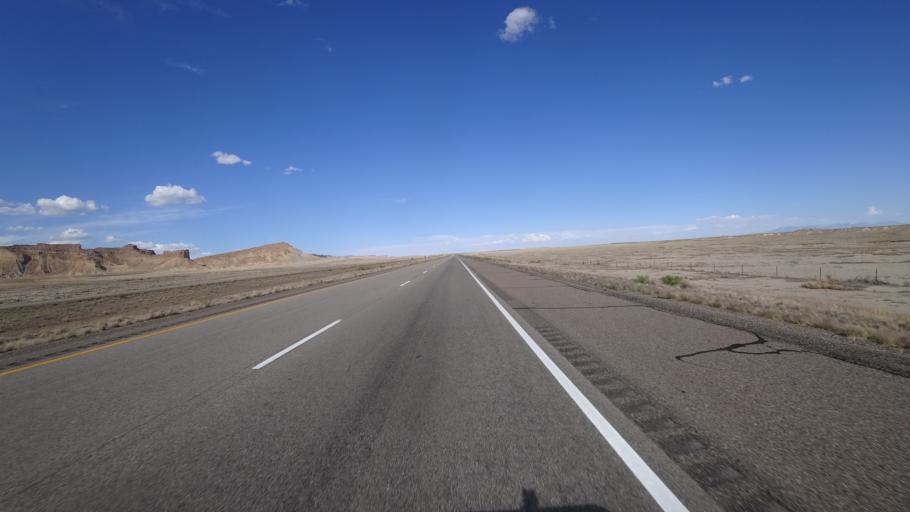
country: US
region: Utah
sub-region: Grand County
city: Moab
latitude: 38.9286
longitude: -109.8850
